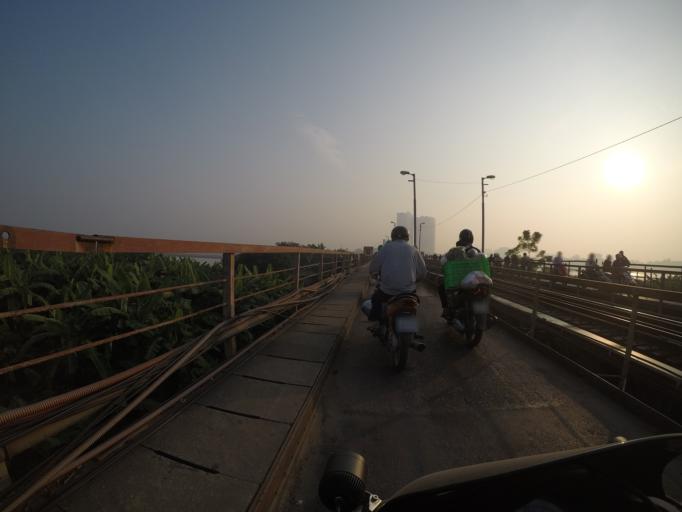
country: VN
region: Ha Noi
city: Hoan Kiem
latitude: 21.0431
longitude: 105.8577
